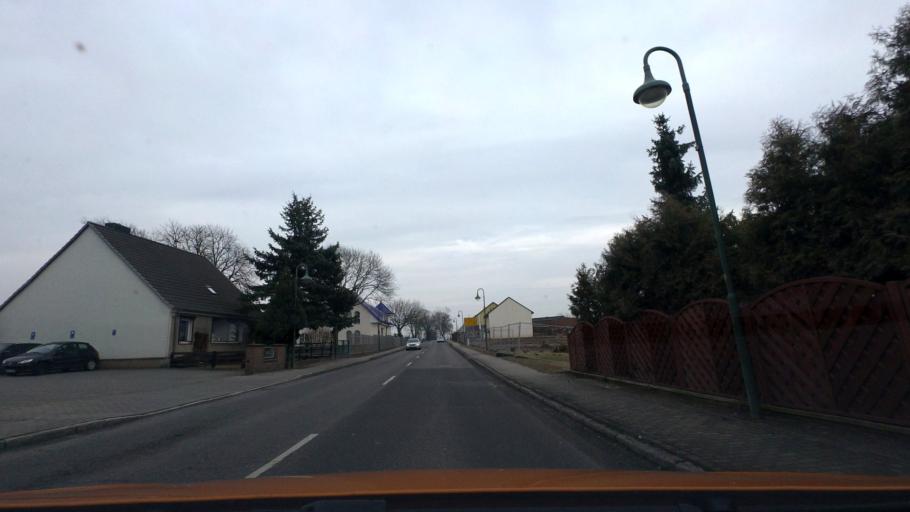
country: DE
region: Brandenburg
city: Ahrensfelde
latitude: 52.5763
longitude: 13.5851
